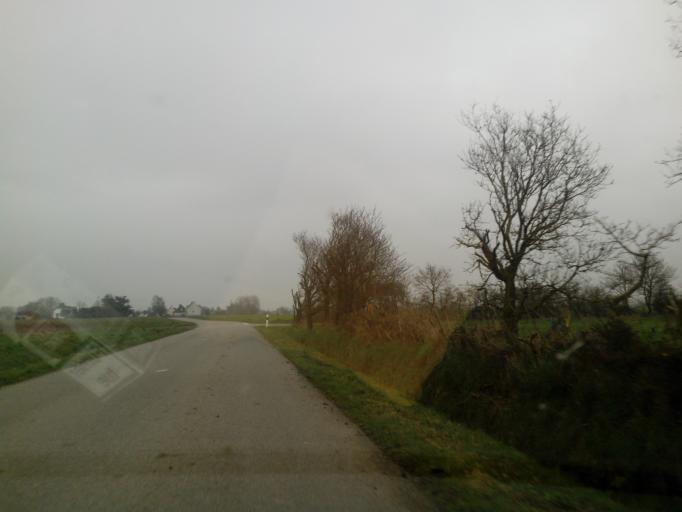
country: FR
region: Brittany
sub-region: Departement du Morbihan
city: Mauron
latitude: 48.0829
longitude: -2.3040
